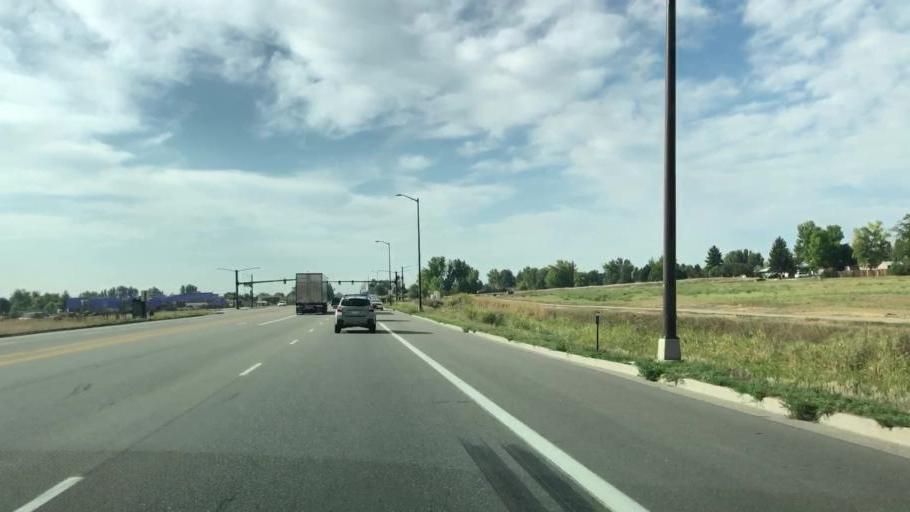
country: US
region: Colorado
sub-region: Larimer County
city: Loveland
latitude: 40.4530
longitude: -105.0775
